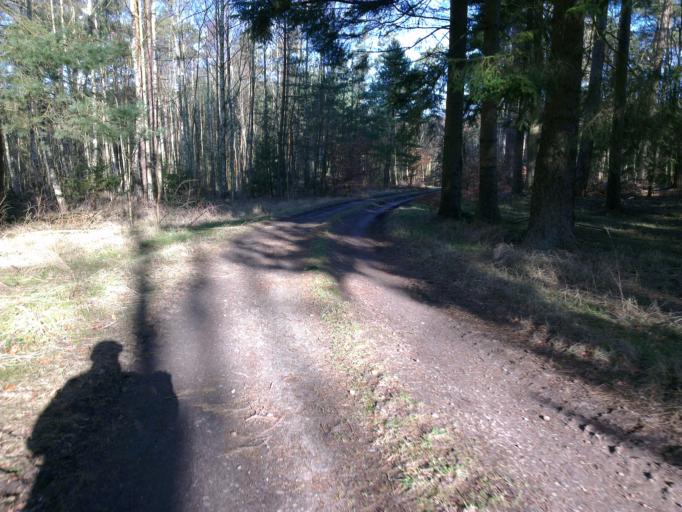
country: DK
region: Capital Region
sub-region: Frederikssund Kommune
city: Jaegerspris
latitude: 55.9035
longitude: 12.0142
